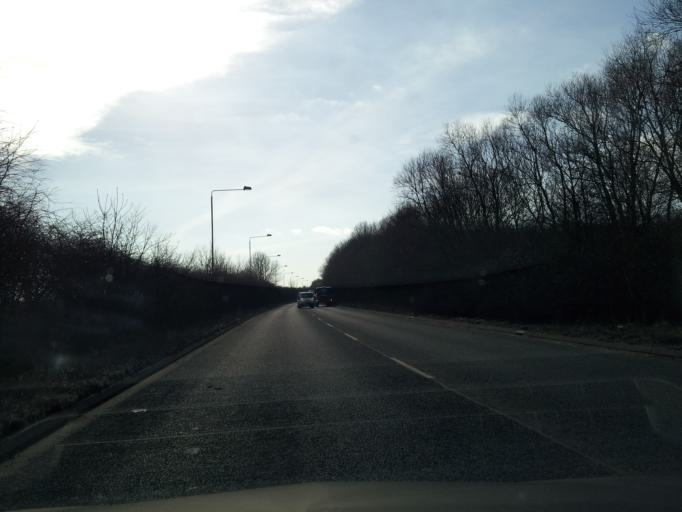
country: GB
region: England
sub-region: Nottinghamshire
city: West Bridgford
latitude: 52.9179
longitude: -1.0995
